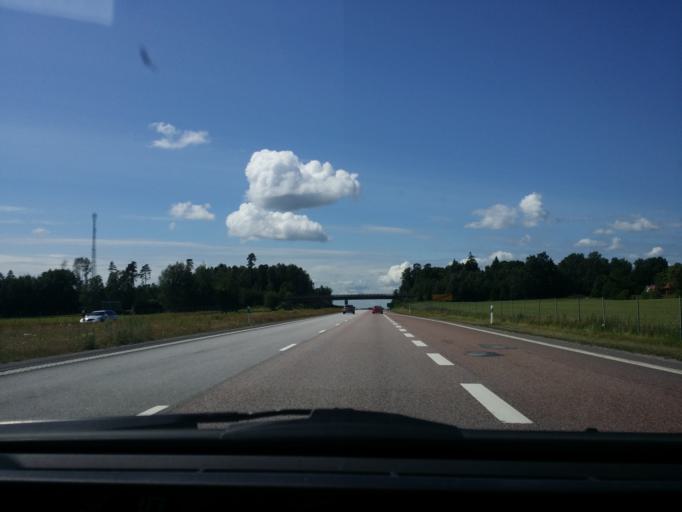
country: SE
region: OErebro
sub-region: Lindesbergs Kommun
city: Frovi
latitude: 59.3089
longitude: 15.4060
